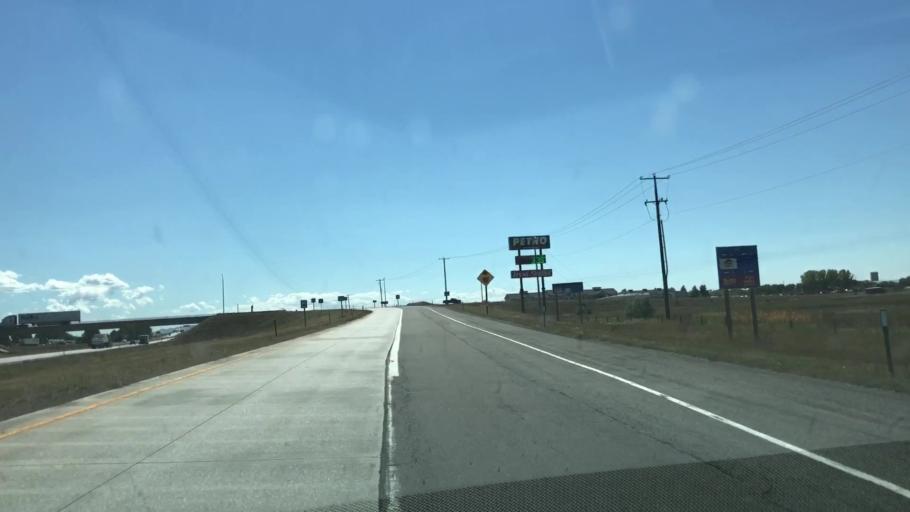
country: US
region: Wyoming
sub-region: Albany County
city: Laramie
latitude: 41.3302
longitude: -105.6165
